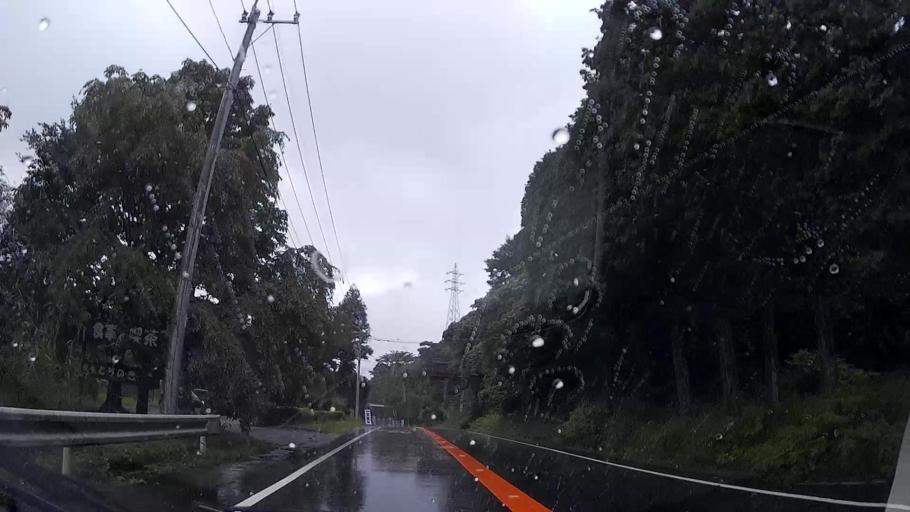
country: JP
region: Kumamoto
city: Aso
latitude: 32.8741
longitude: 130.9922
